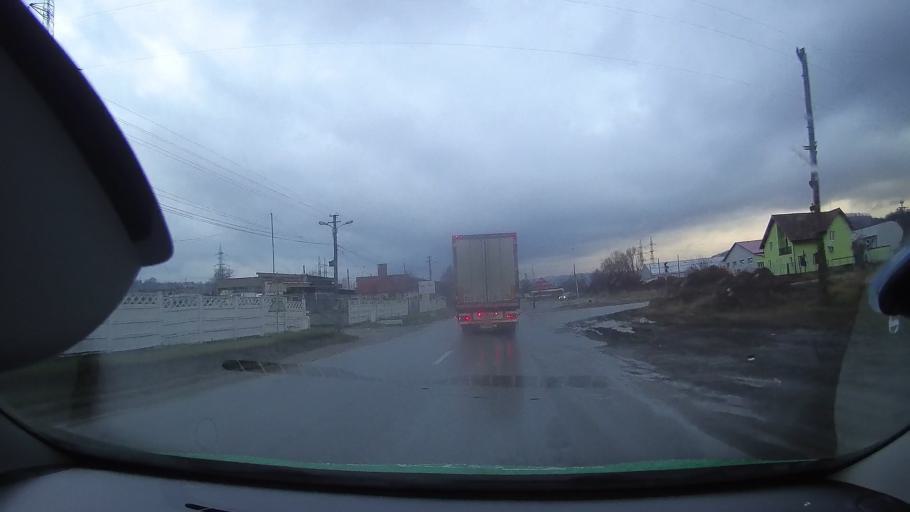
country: RO
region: Hunedoara
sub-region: Municipiul Brad
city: Brad
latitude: 46.1421
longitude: 22.7761
